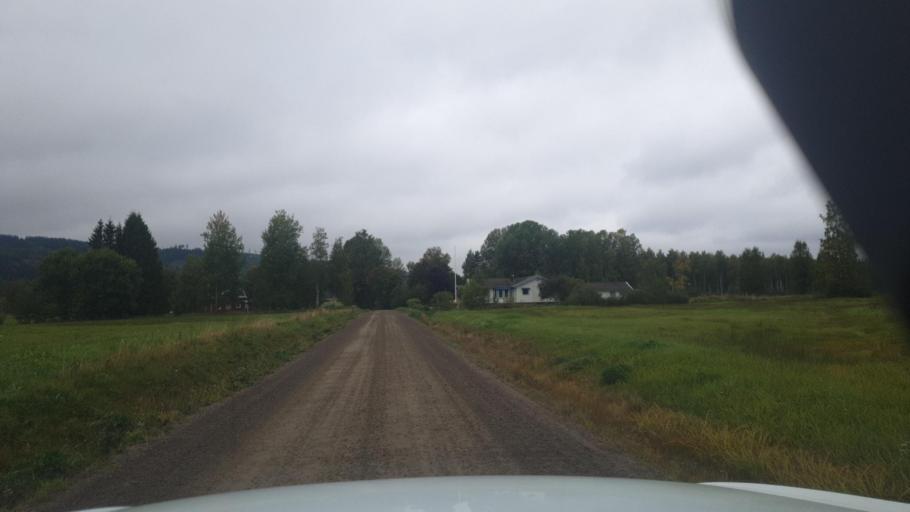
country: SE
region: Vaermland
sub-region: Sunne Kommun
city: Sunne
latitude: 59.8165
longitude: 13.0435
